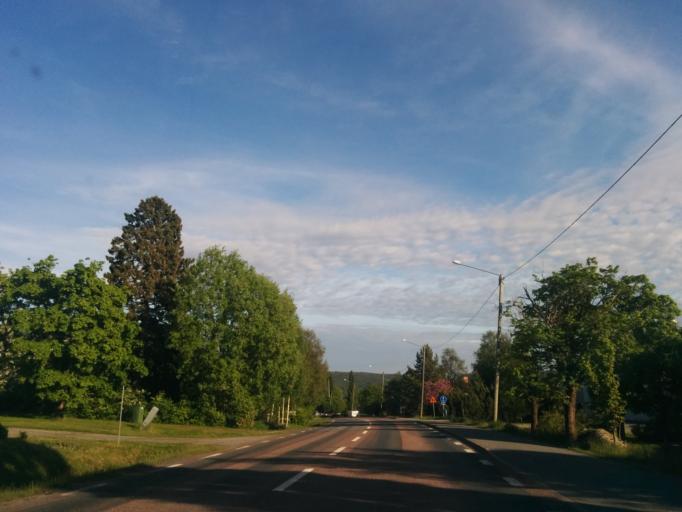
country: SE
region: Vaesternorrland
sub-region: Kramfors Kommun
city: Kramfors
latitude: 62.9740
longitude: 17.8835
